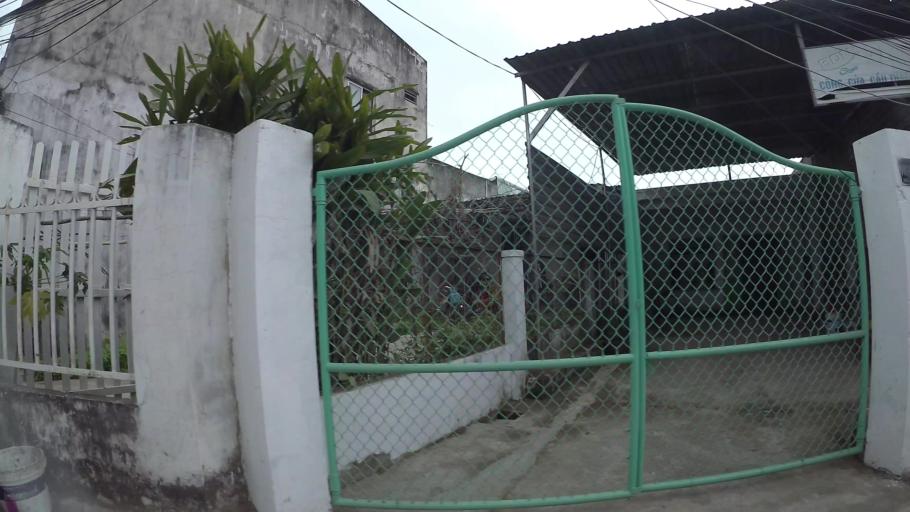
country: VN
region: Da Nang
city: Lien Chieu
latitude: 16.0508
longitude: 108.1577
